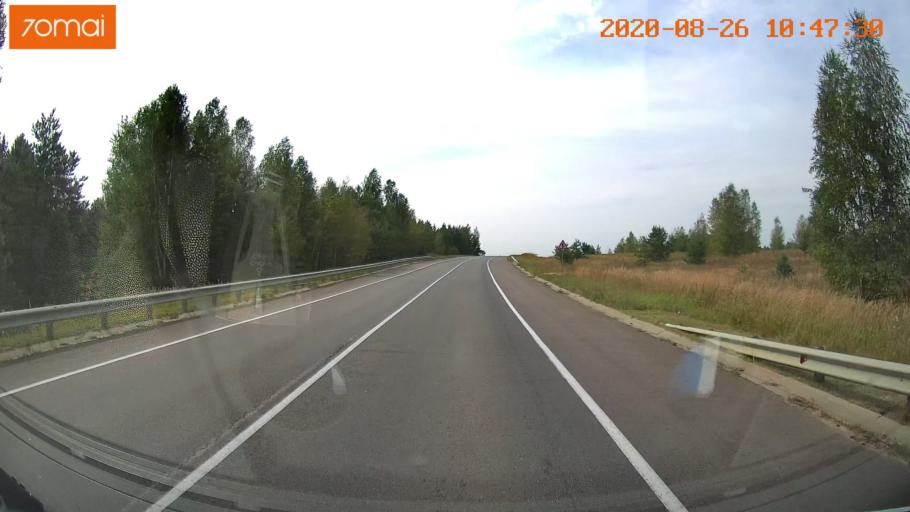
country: RU
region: Rjazan
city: Lashma
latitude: 54.7260
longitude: 41.1888
